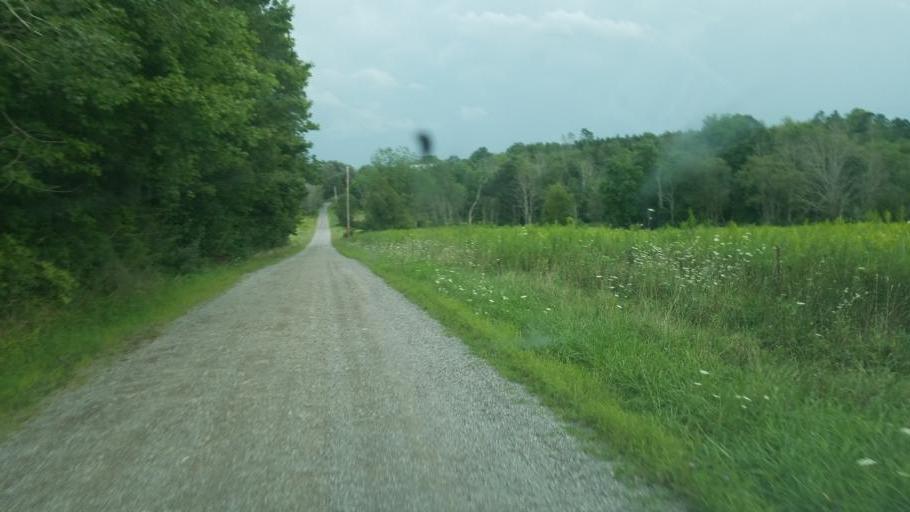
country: US
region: Pennsylvania
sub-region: Clarion County
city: Knox
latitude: 41.1498
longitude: -79.5201
